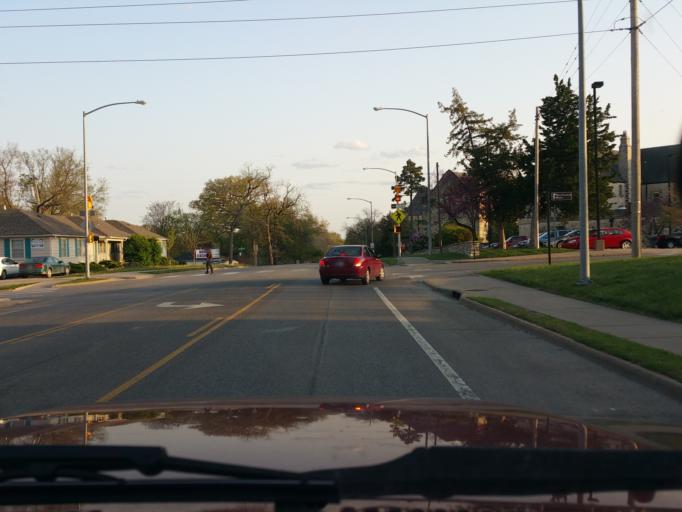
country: US
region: Kansas
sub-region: Riley County
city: Manhattan
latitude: 39.1935
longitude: -96.5764
